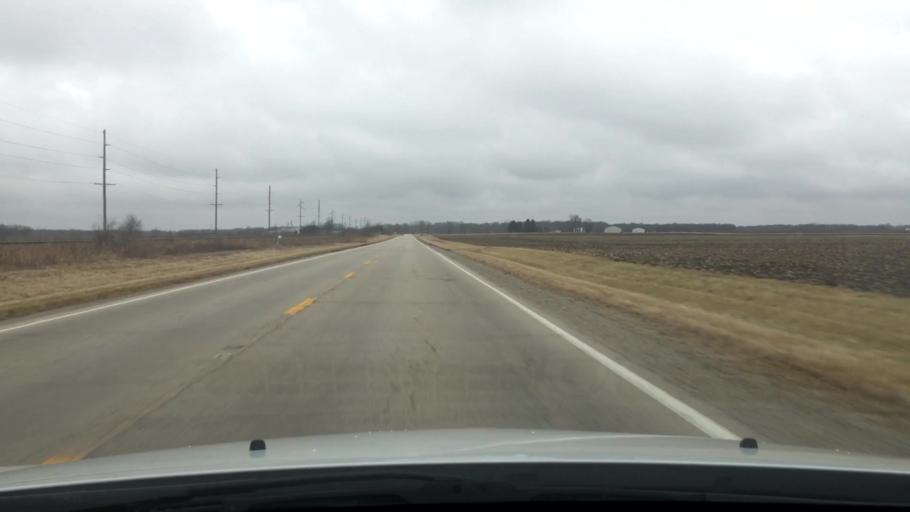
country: US
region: Illinois
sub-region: Iroquois County
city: Sheldon
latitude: 40.8001
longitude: -87.5725
